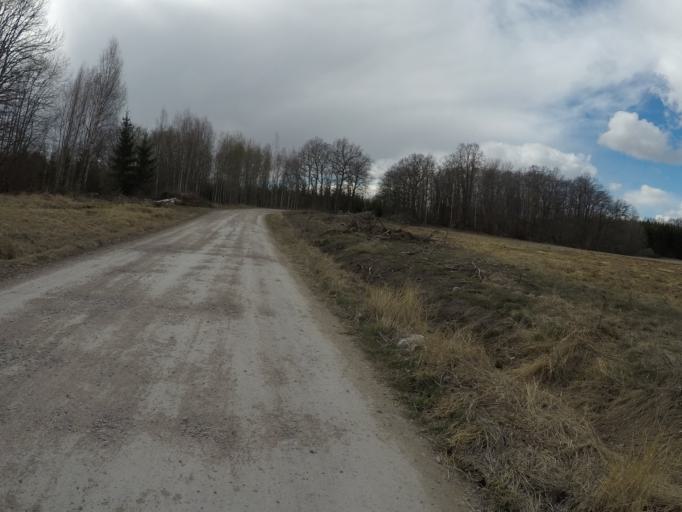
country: SE
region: Soedermanland
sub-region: Eskilstuna Kommun
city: Kvicksund
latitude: 59.4696
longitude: 16.3143
